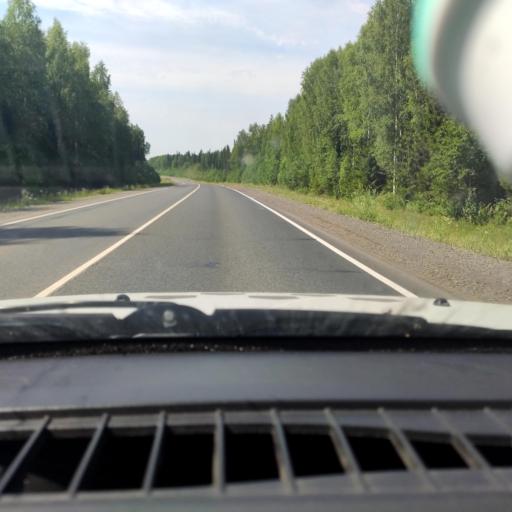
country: RU
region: Perm
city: Zyukayka
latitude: 58.3811
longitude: 54.6134
